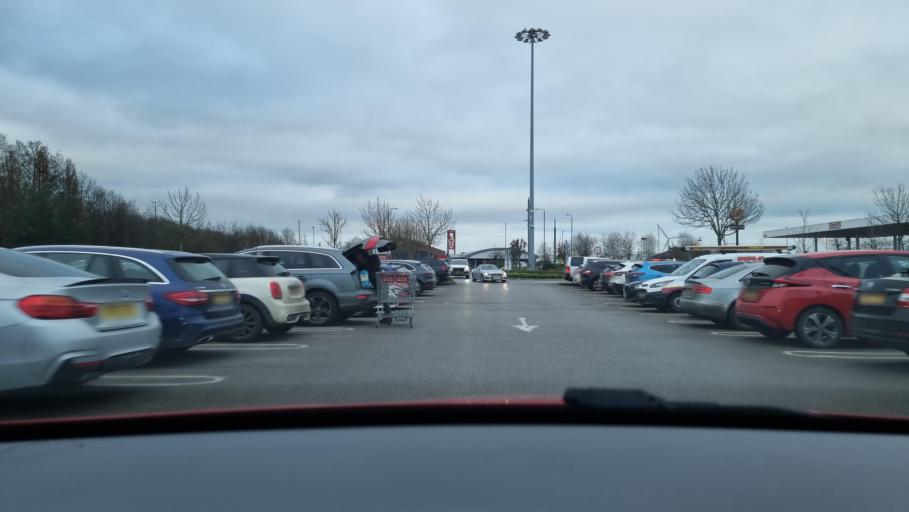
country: GB
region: England
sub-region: Derby
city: Derby
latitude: 52.9191
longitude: -1.4440
